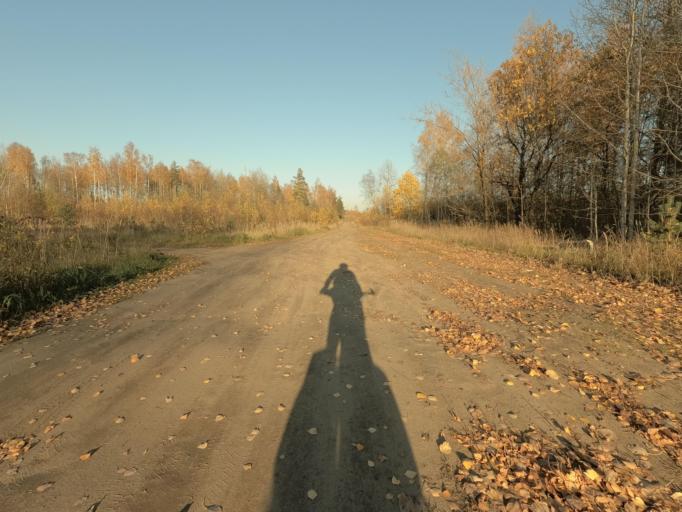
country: RU
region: Leningrad
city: Kirovsk
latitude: 59.8594
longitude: 31.0065
